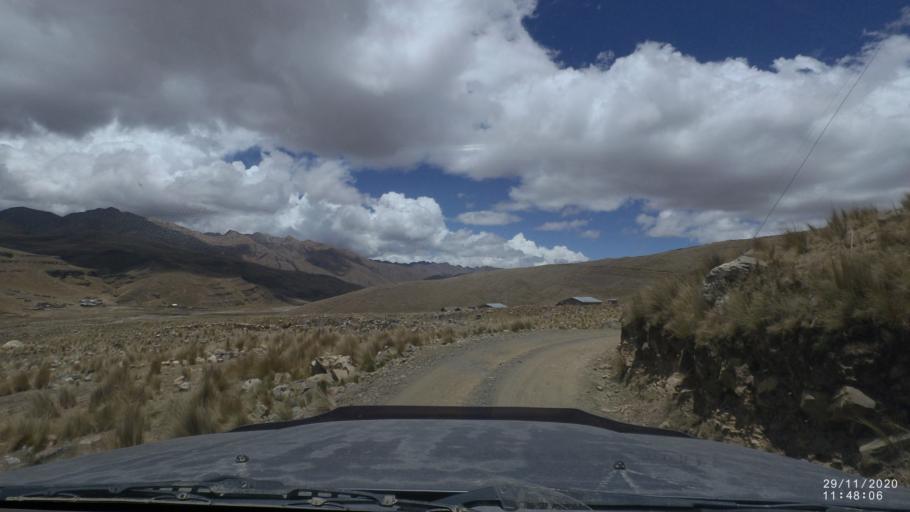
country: BO
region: Cochabamba
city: Cochabamba
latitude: -17.1808
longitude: -66.2559
